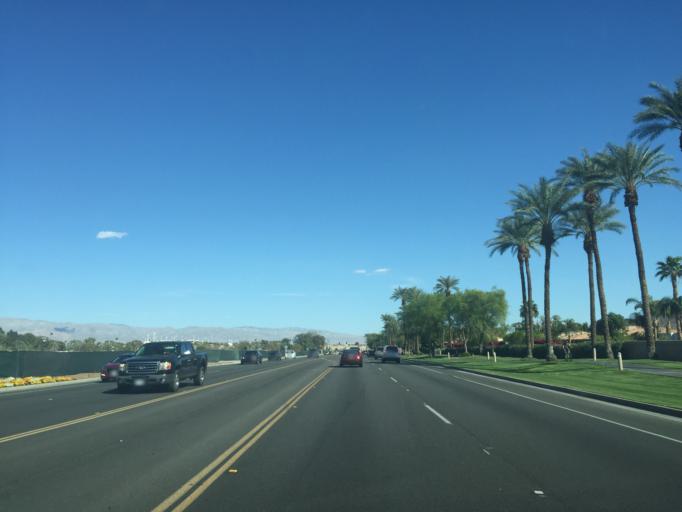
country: US
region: California
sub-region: Riverside County
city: Indian Wells
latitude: 33.7213
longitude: -116.3221
